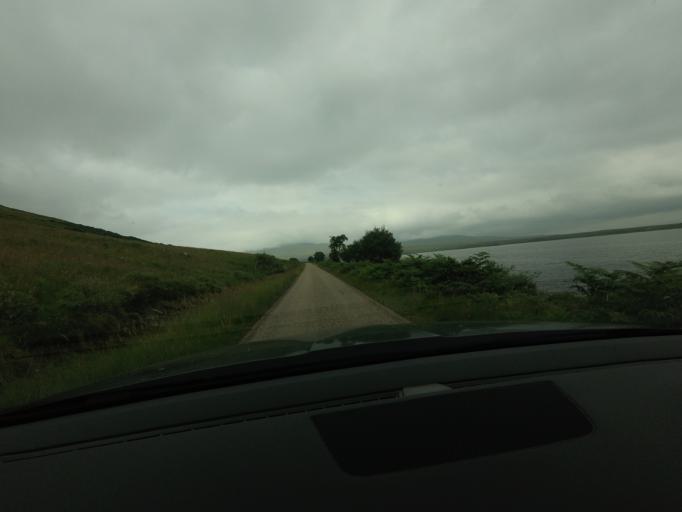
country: GB
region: Scotland
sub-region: Highland
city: Golspie
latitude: 58.3751
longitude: -4.3682
